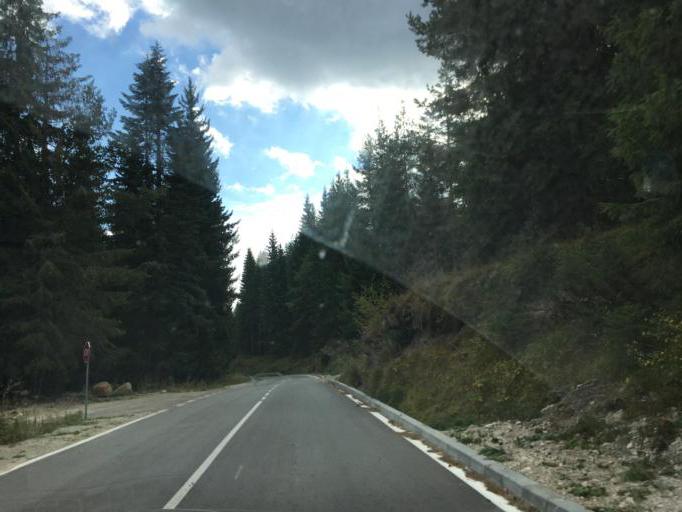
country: BG
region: Pazardzhik
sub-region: Obshtina Batak
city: Batak
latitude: 41.9039
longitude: 24.3011
